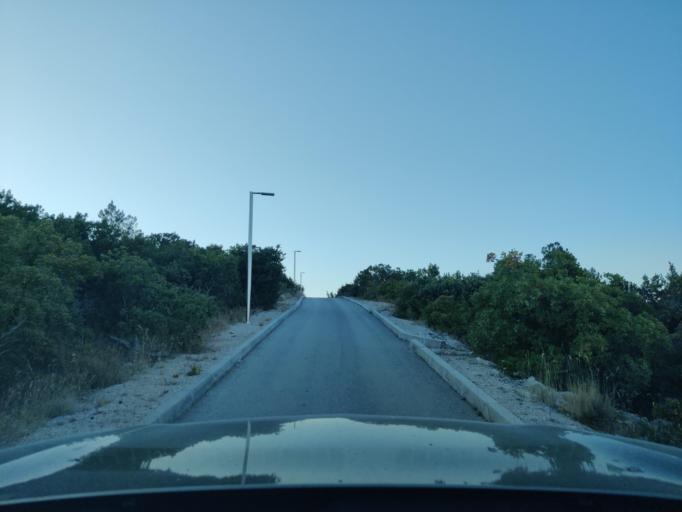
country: HR
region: Sibensko-Kniniska
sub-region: Grad Sibenik
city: Tisno
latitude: 43.8100
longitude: 15.6282
